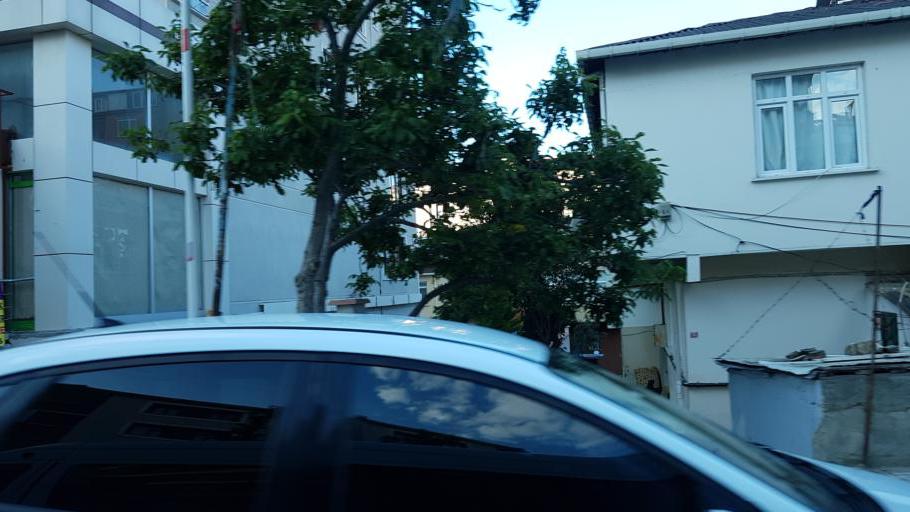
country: TR
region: Istanbul
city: Maltepe
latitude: 40.9422
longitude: 29.1516
